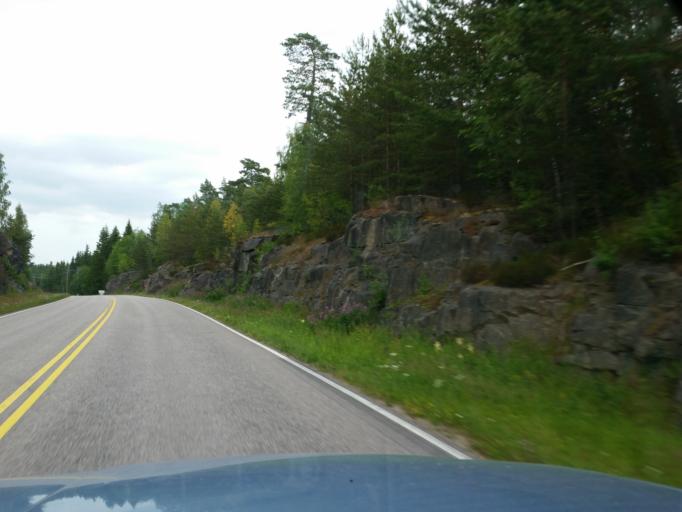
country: FI
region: Varsinais-Suomi
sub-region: Aboland-Turunmaa
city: Nagu
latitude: 60.1734
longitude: 21.9579
